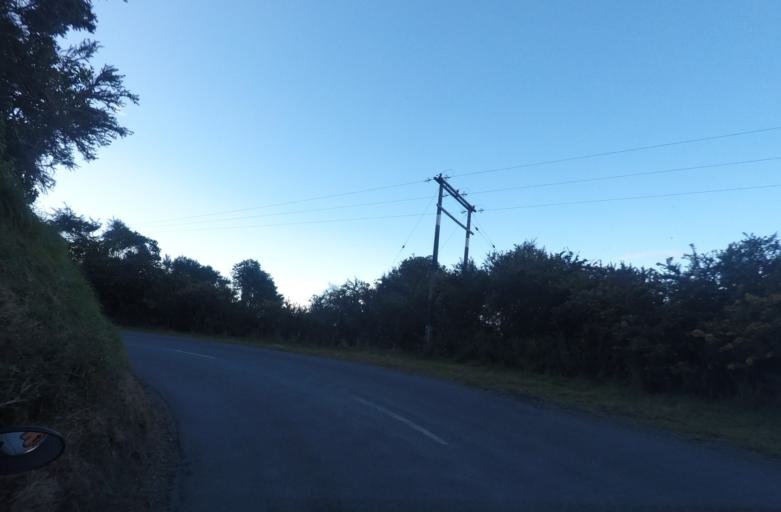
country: NZ
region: Marlborough
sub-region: Marlborough District
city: Picton
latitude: -41.2712
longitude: 173.9586
